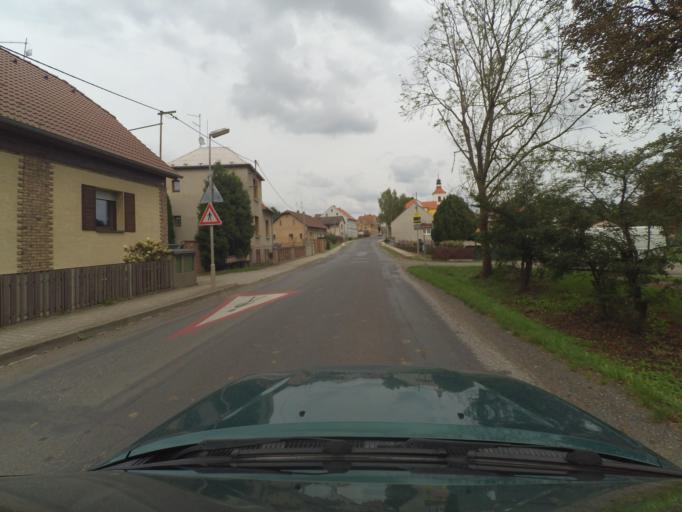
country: CZ
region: Central Bohemia
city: Luzna
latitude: 50.1467
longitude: 13.7392
